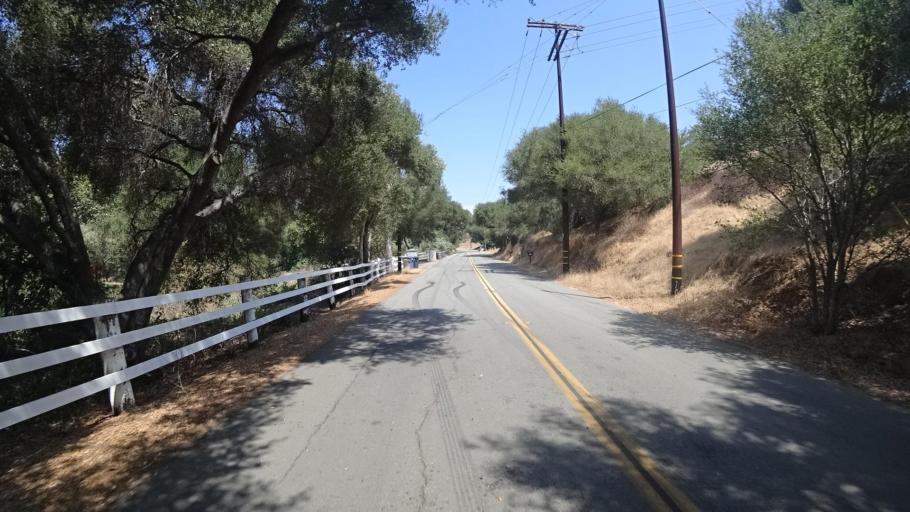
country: US
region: California
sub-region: San Diego County
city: Bonsall
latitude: 33.3188
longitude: -117.2364
